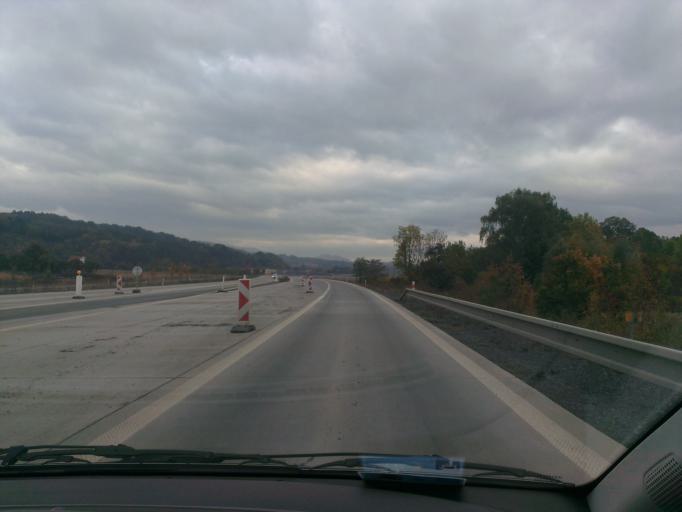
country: CZ
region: Zlin
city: Lesna
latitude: 49.5095
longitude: 17.9337
